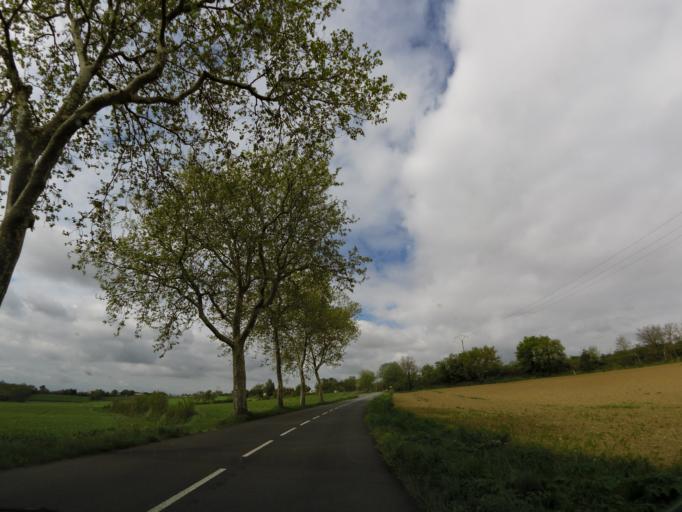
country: FR
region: Languedoc-Roussillon
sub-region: Departement de l'Aude
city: Saint-Martin-Lalande
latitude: 43.3279
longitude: 2.0269
